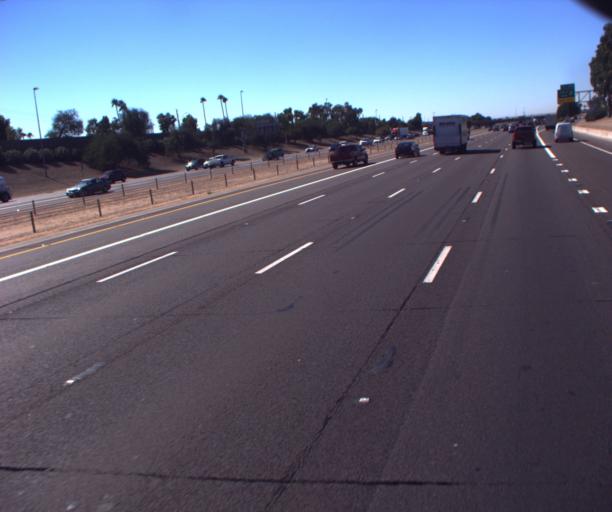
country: US
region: Arizona
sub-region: Maricopa County
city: Phoenix
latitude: 33.4620
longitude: -112.1453
